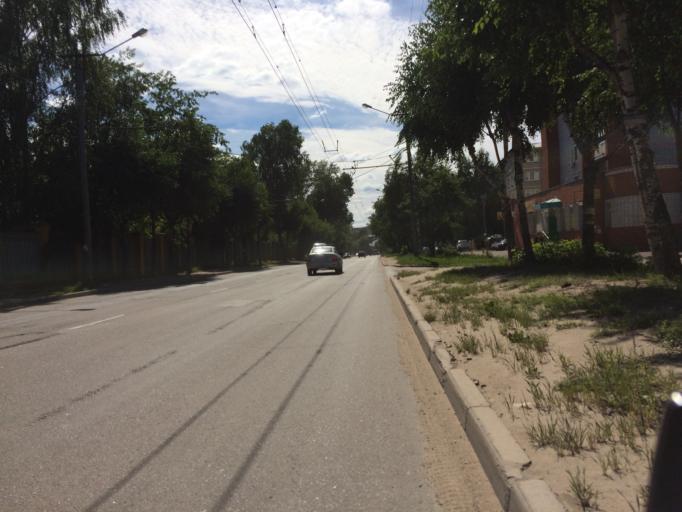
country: RU
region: Mariy-El
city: Yoshkar-Ola
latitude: 56.6373
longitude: 47.9470
